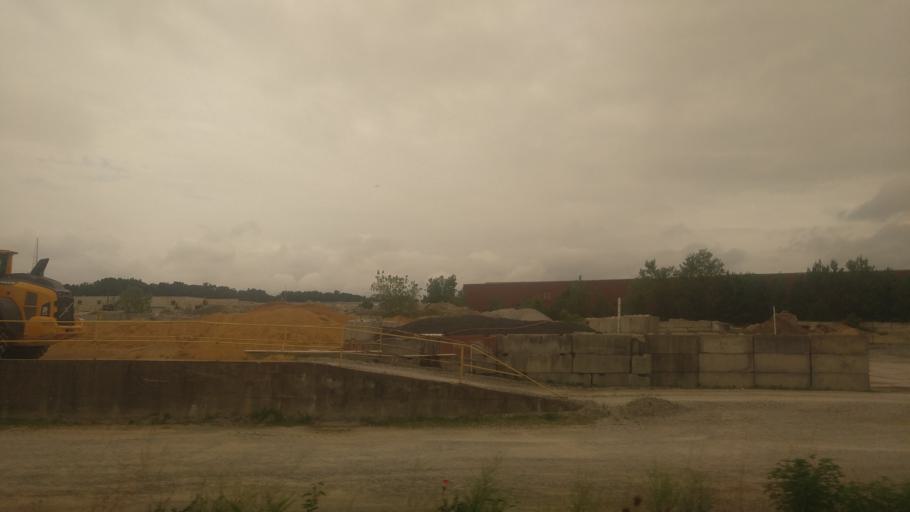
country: US
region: Virginia
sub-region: Henrico County
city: Dumbarton
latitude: 37.5922
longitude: -77.4833
